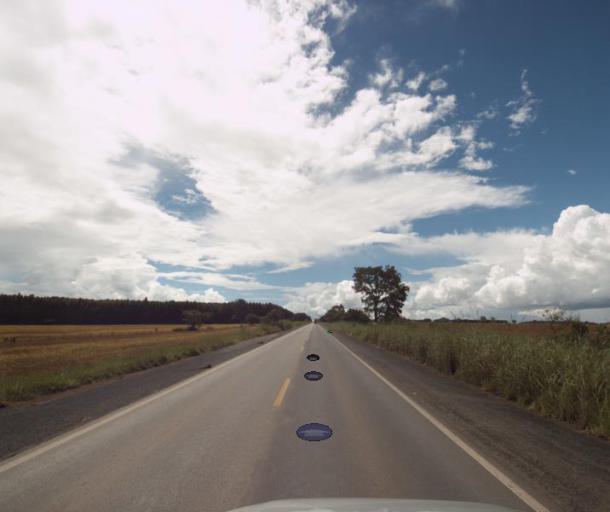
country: BR
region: Goias
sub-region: Uruacu
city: Uruacu
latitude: -14.1776
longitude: -49.1256
